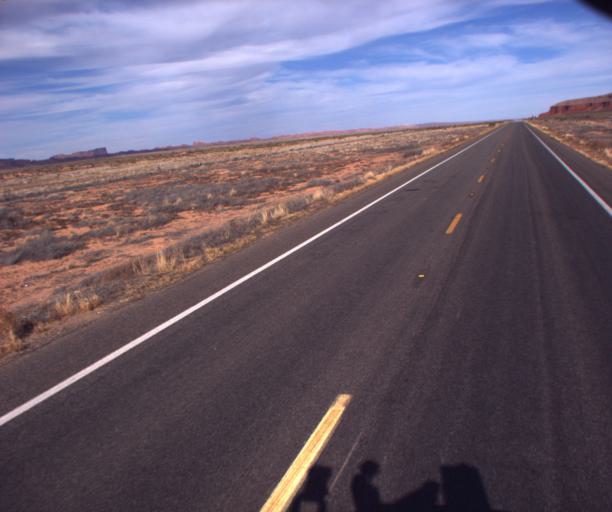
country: US
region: Arizona
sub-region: Navajo County
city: Kayenta
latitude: 36.7537
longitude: -110.0564
